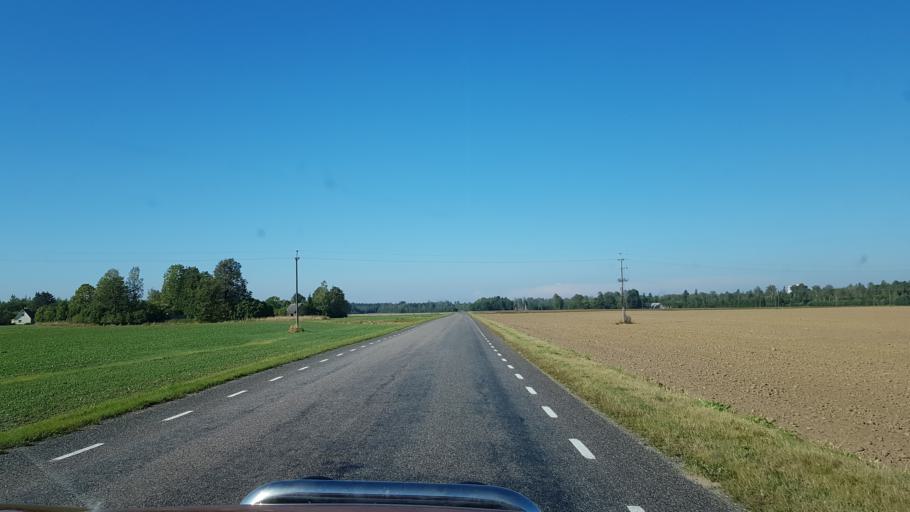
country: EE
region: Jogevamaa
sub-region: Jogeva linn
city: Jogeva
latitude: 58.7003
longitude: 26.3961
